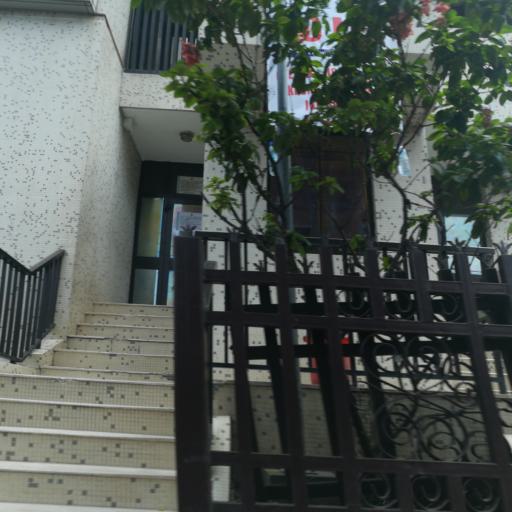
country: NG
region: Lagos
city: Lagos
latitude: 6.4523
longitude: 3.3935
